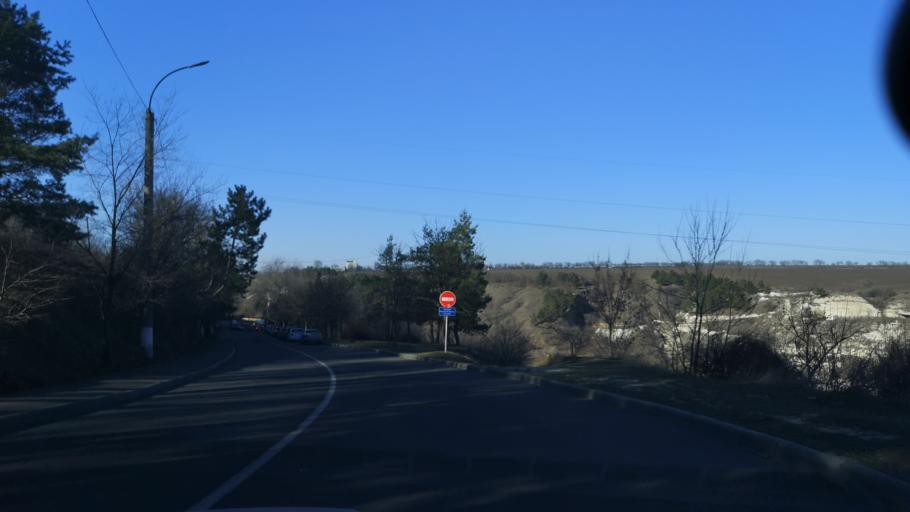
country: MD
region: Chisinau
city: Cricova
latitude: 47.1466
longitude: 28.8630
